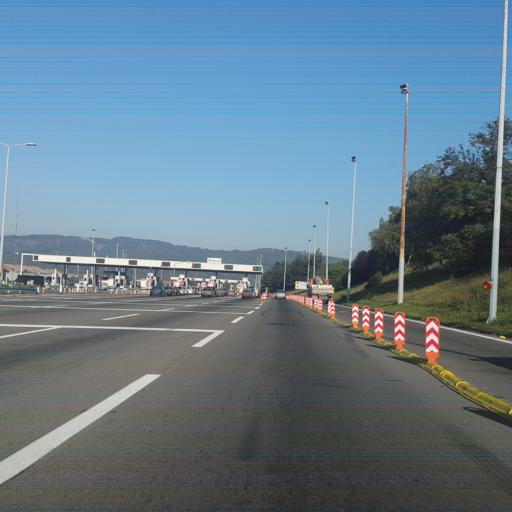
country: RS
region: Central Serbia
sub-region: Belgrade
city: Zvezdara
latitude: 44.7166
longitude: 20.5576
